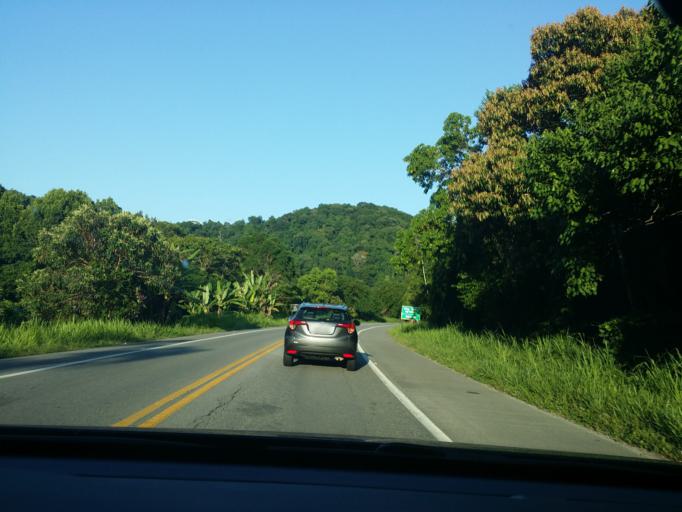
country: BR
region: Sao Paulo
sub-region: Sao Sebastiao
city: Sao Sebastiao
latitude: -23.7679
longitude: -45.6961
